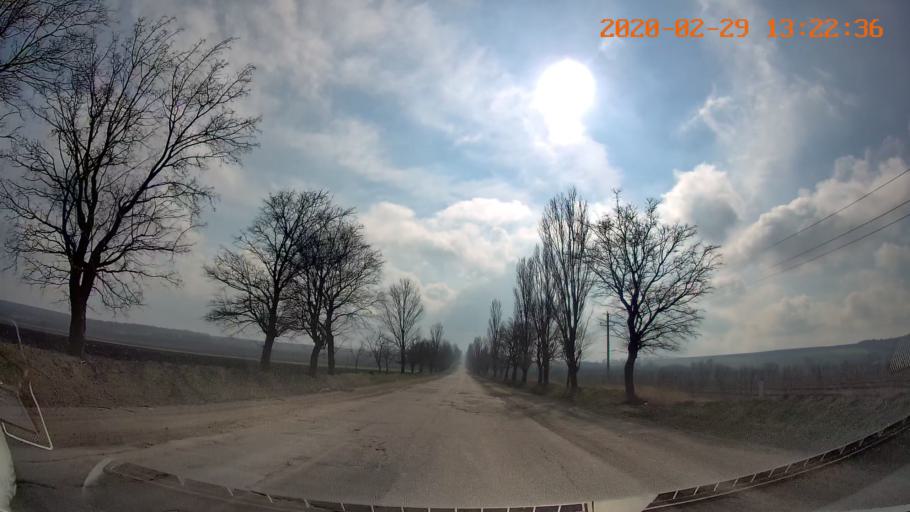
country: MD
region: Telenesti
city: Camenca
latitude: 47.9586
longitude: 28.6275
